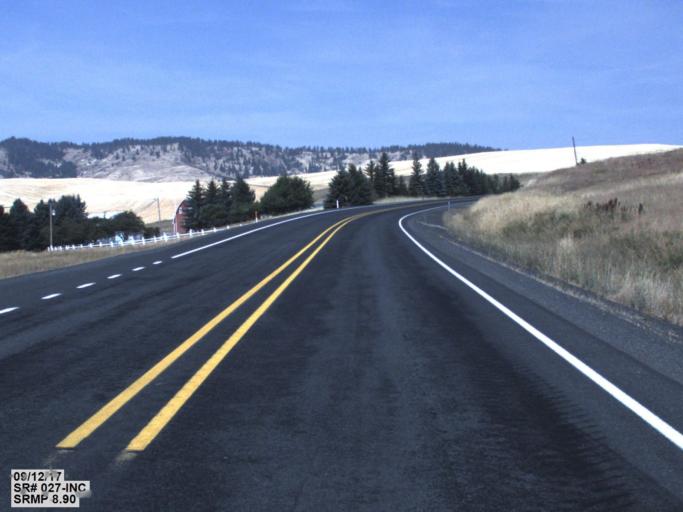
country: US
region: Washington
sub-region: Whitman County
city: Pullman
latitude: 46.8412
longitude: -117.1242
